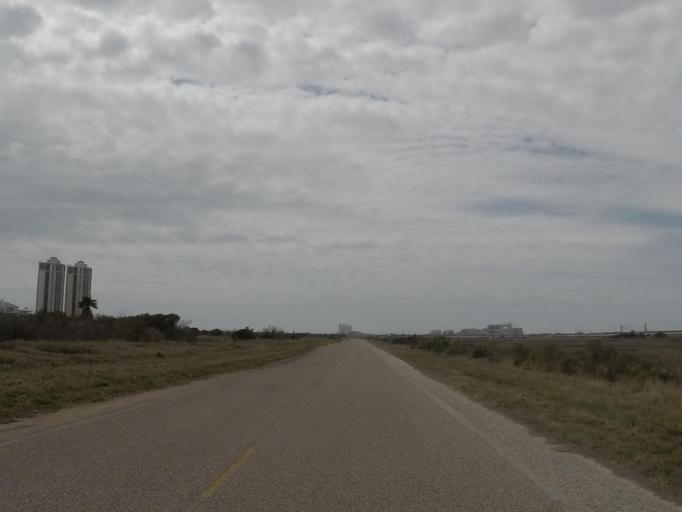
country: US
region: Texas
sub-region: Galveston County
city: Galveston
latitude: 29.3238
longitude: -94.7508
